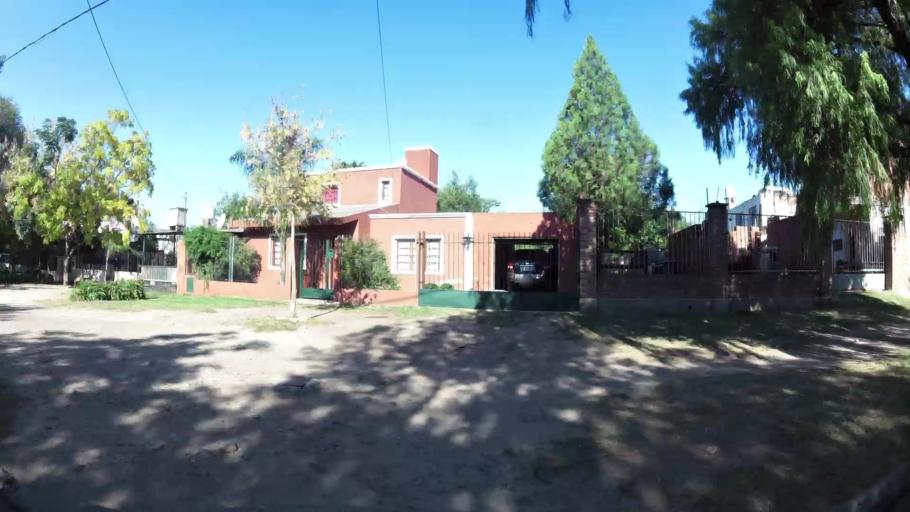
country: AR
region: Cordoba
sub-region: Departamento de Capital
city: Cordoba
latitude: -31.3758
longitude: -64.2488
